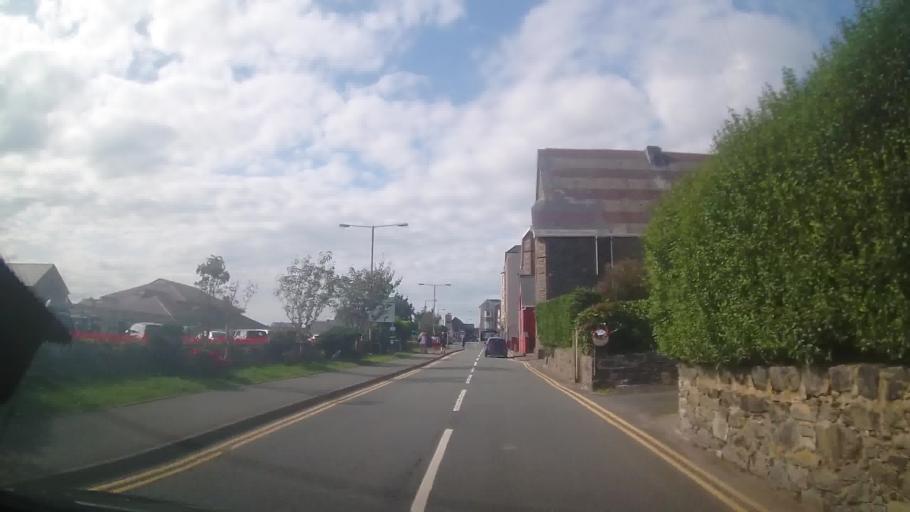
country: GB
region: Wales
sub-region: Gwynedd
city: Barmouth
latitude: 52.7210
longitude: -4.0543
